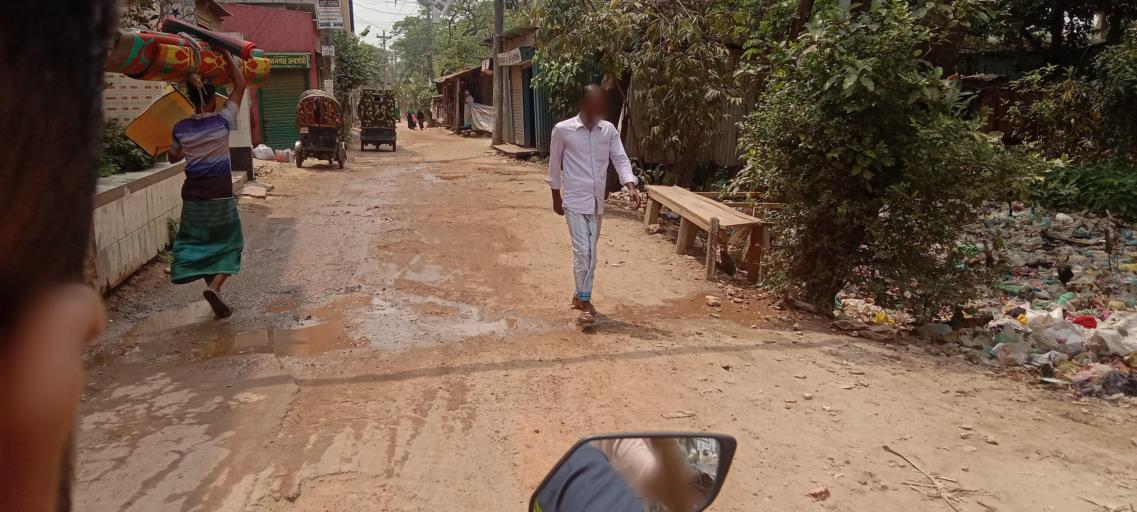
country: BD
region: Dhaka
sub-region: Dhaka
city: Dhaka
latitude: 23.6781
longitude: 90.4199
